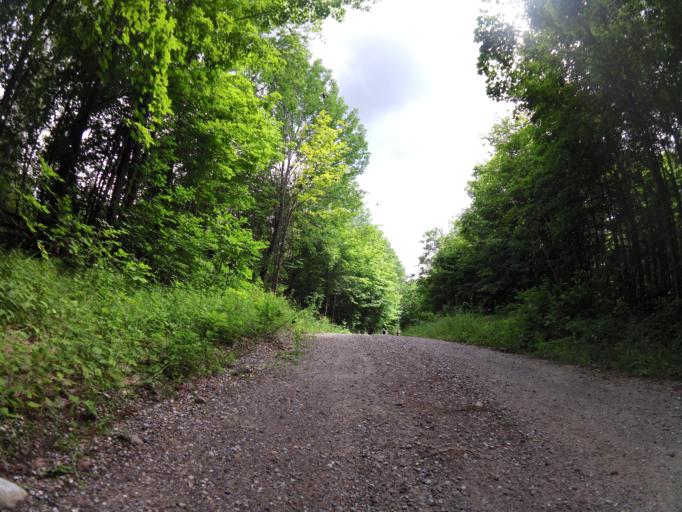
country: CA
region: Ontario
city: Perth
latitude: 45.0219
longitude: -76.5547
